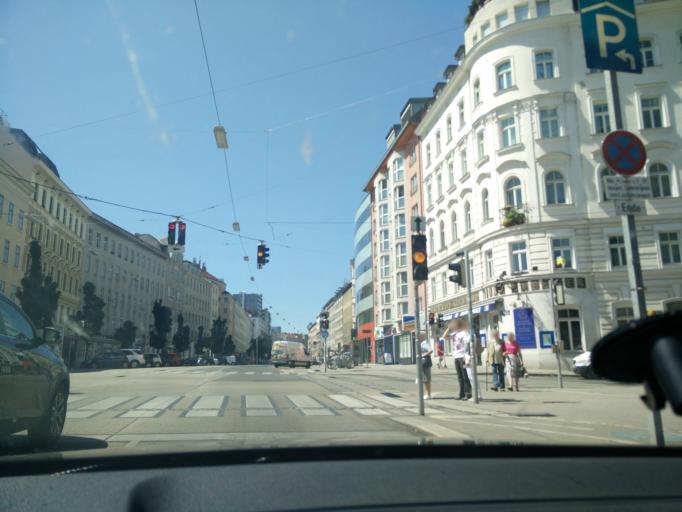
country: AT
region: Vienna
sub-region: Wien Stadt
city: Vienna
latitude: 48.1853
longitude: 16.3623
